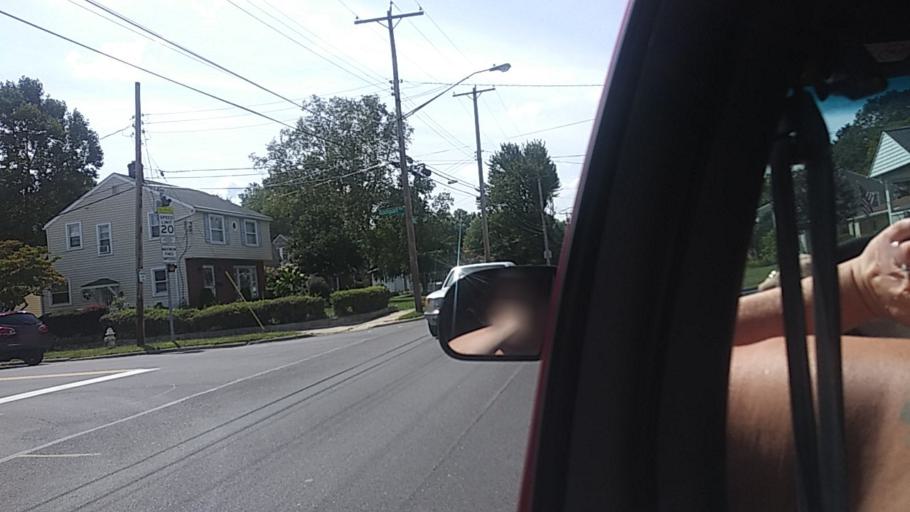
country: US
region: Ohio
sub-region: Summit County
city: Fairlawn
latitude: 41.1196
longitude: -81.5666
